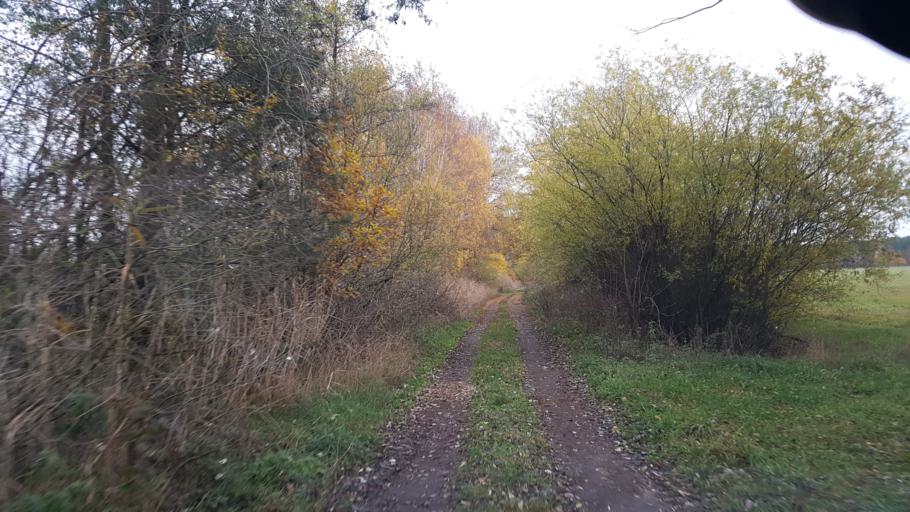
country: DE
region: Brandenburg
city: Sallgast
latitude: 51.6209
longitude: 13.8837
